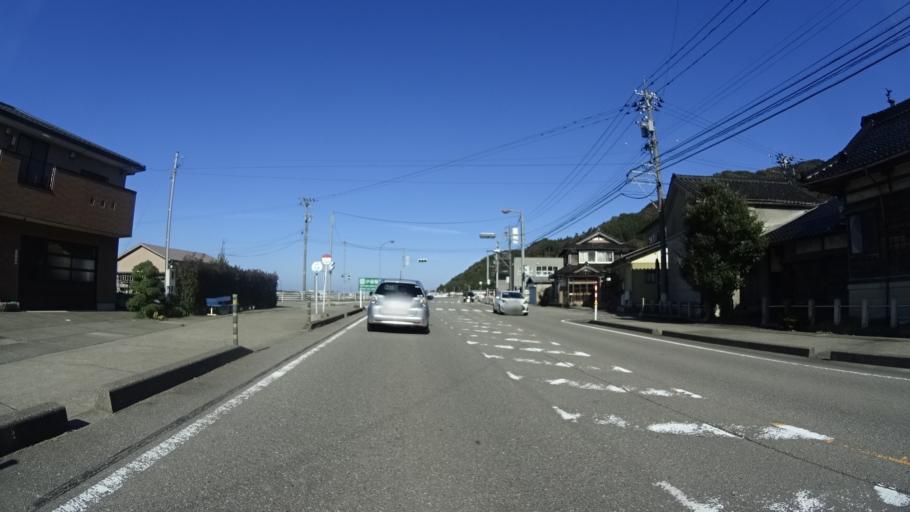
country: JP
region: Ishikawa
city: Tsurugi-asahimachi
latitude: 36.4605
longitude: 136.6211
